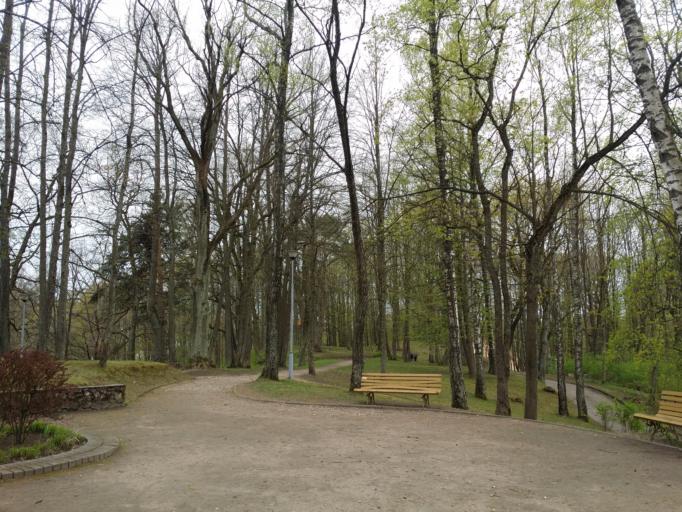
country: LT
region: Vilnius County
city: Rasos
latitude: 54.6737
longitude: 25.3255
